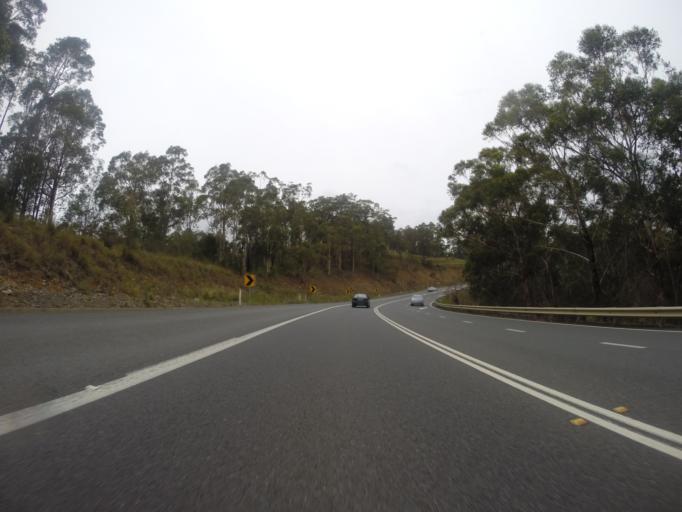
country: AU
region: New South Wales
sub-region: Eurobodalla
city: Batemans Bay
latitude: -35.7312
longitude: 150.1700
